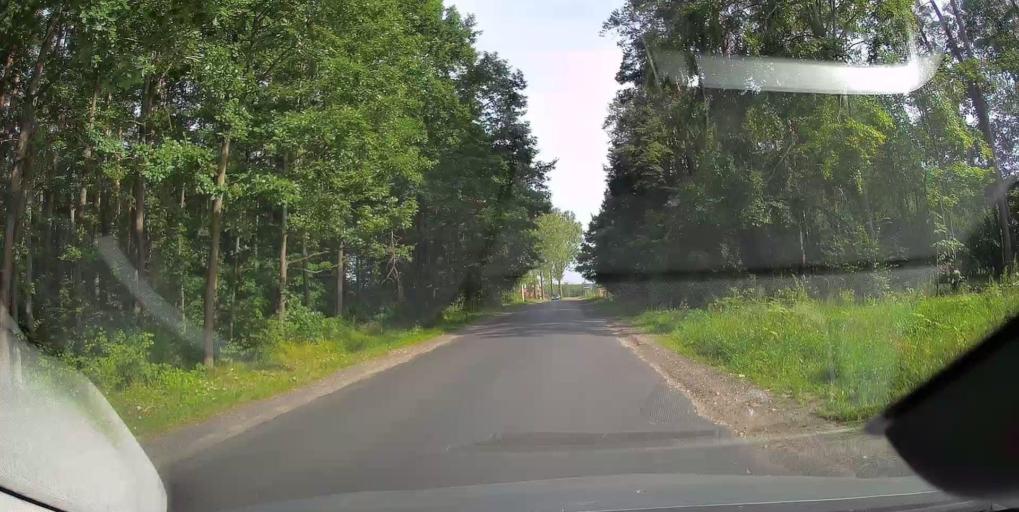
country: PL
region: Lodz Voivodeship
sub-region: Powiat tomaszowski
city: Tomaszow Mazowiecki
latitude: 51.4628
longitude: 20.0309
